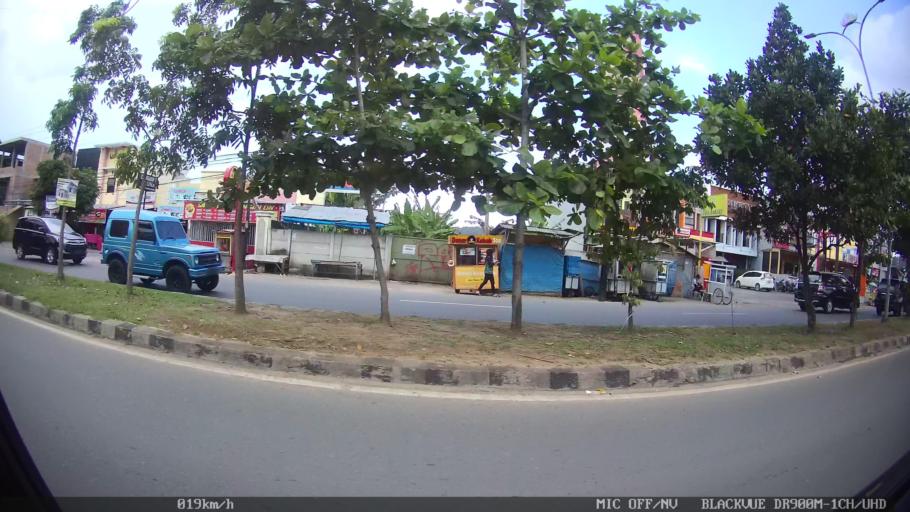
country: ID
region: Lampung
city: Kedaton
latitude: -5.3973
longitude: 105.2128
